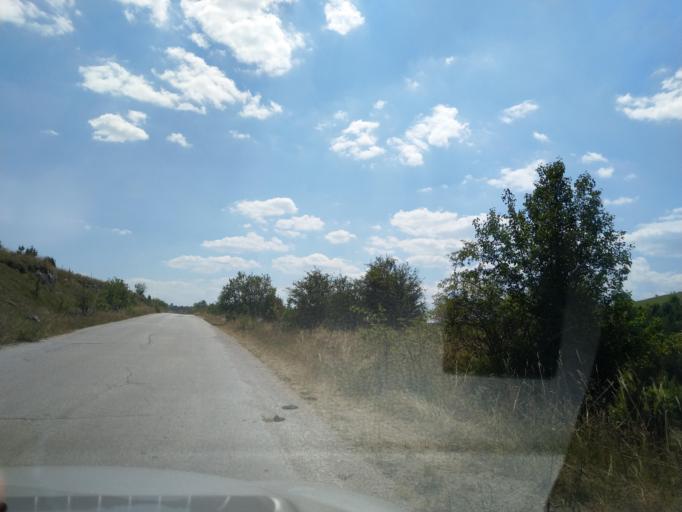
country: RS
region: Central Serbia
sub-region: Zlatiborski Okrug
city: Nova Varos
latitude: 43.4438
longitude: 19.9564
